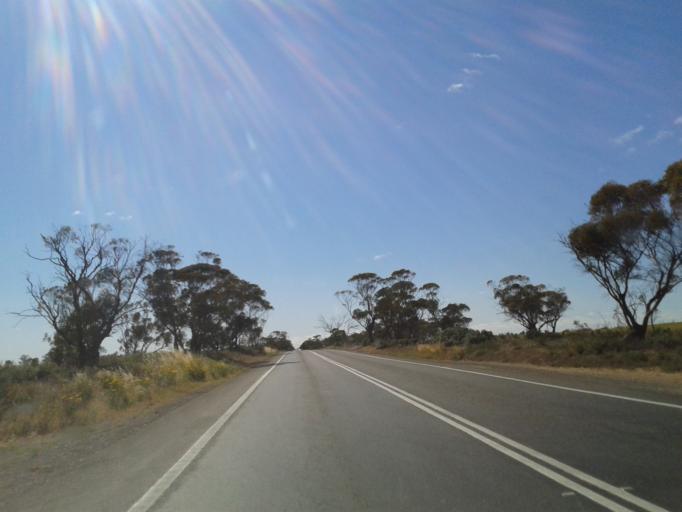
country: AU
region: South Australia
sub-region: Renmark Paringa
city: Renmark
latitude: -34.2759
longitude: 141.3675
